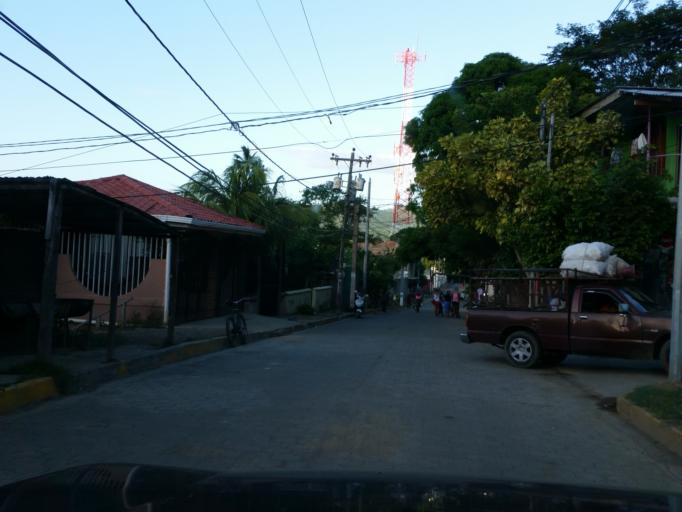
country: NI
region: Rivas
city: San Juan del Sur
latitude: 11.2491
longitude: -85.8735
